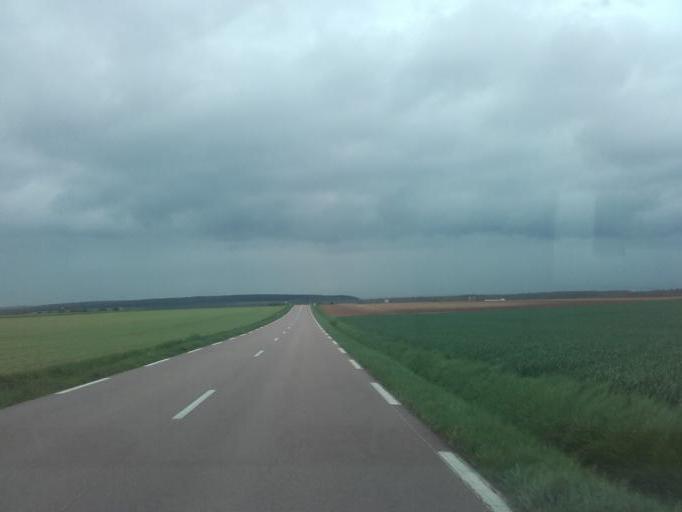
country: FR
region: Bourgogne
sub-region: Departement de l'Yonne
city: Joux-la-Ville
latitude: 47.7191
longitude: 3.8530
